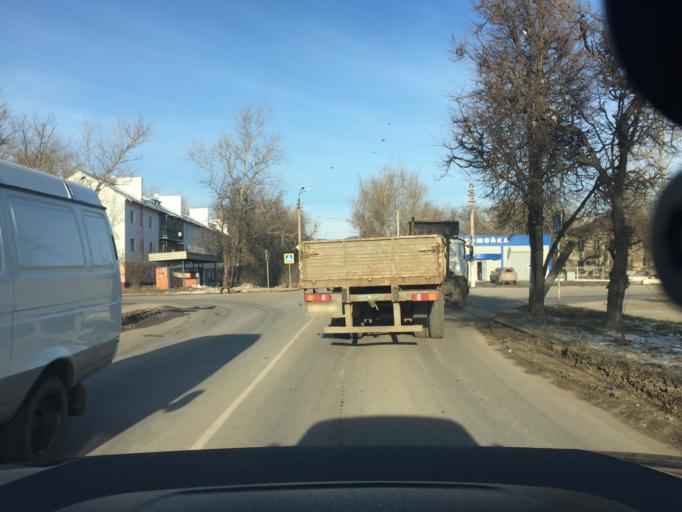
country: RU
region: Tula
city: Tula
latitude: 54.1777
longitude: 37.7051
